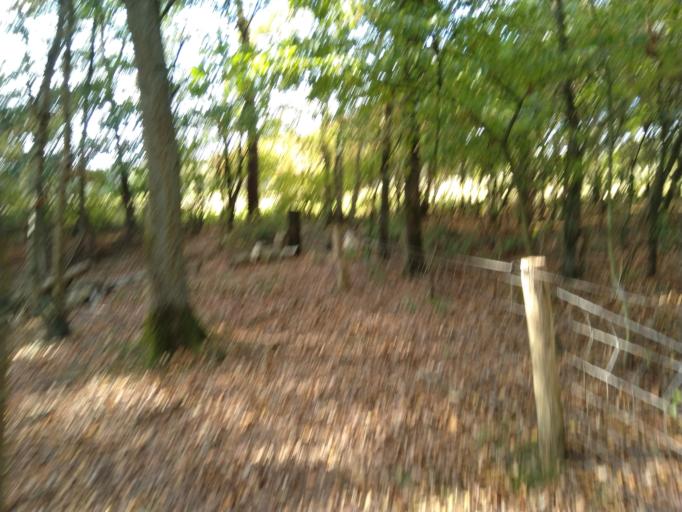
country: NL
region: Drenthe
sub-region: Gemeente Aa en Hunze
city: Anloo
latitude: 53.0497
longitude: 6.6557
